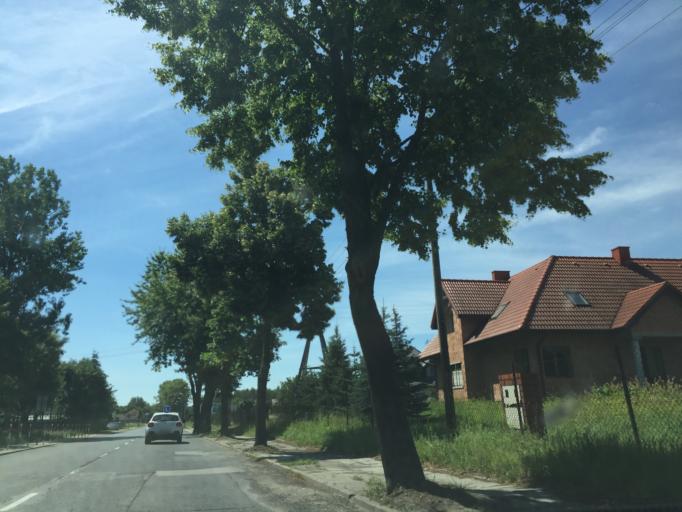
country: PL
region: Lodz Voivodeship
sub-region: Piotrkow Trybunalski
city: Piotrkow Trybunalski
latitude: 51.4186
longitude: 19.7129
